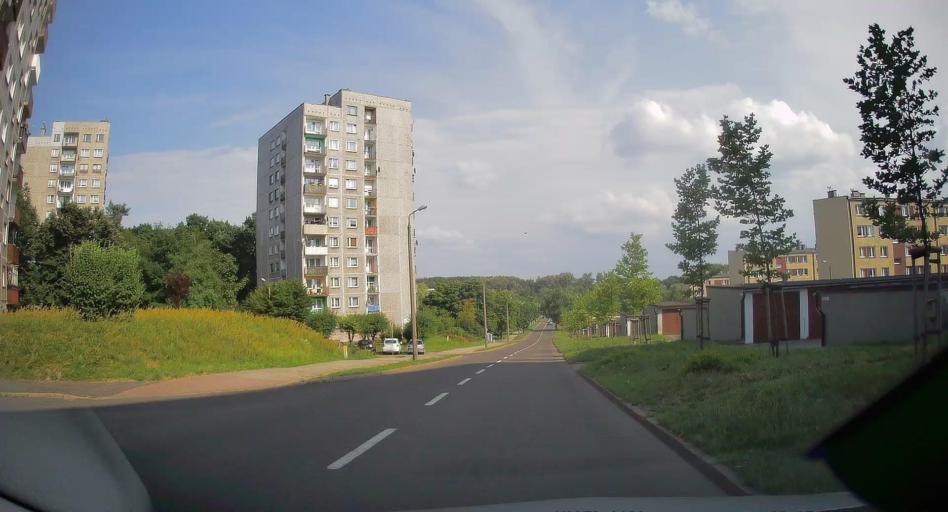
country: PL
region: Silesian Voivodeship
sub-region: Swietochlowice
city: Swietochlowice
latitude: 50.3117
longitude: 18.9164
